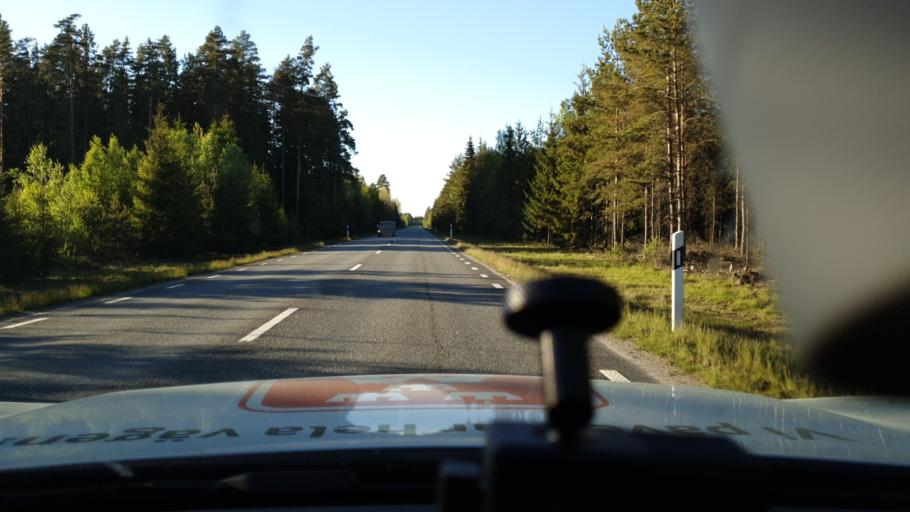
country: SE
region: Joenkoeping
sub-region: Eksjo Kommun
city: Eksjoe
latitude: 57.6201
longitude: 14.9699
